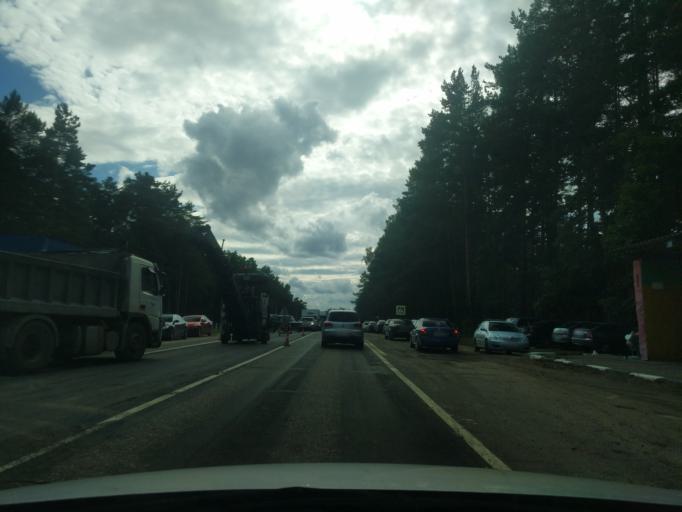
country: RU
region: Jaroslavl
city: Levashevo
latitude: 57.6758
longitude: 40.5878
